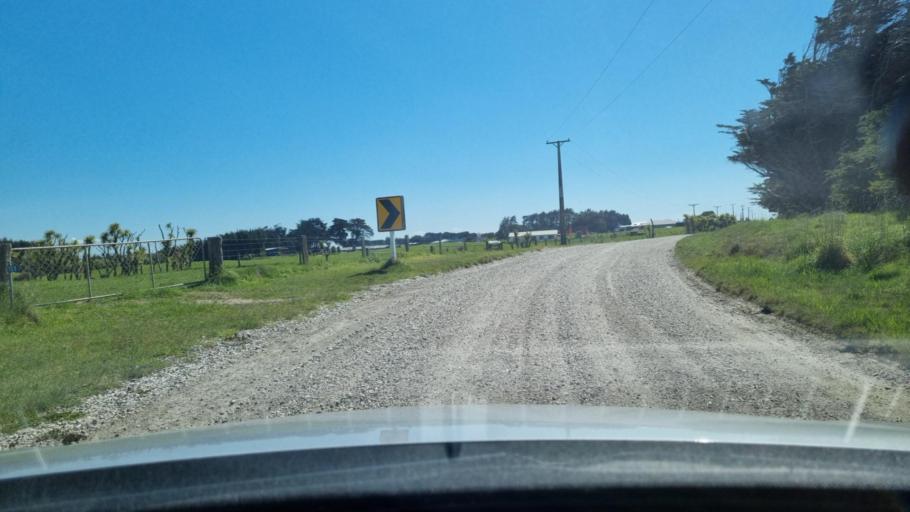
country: NZ
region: Southland
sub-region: Invercargill City
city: Invercargill
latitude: -46.4153
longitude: 168.2635
